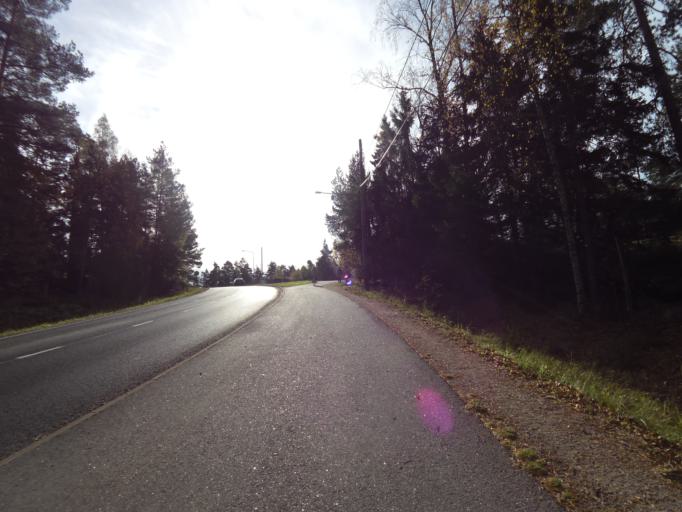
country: FI
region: Uusimaa
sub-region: Helsinki
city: Espoo
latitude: 60.1310
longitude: 24.6803
